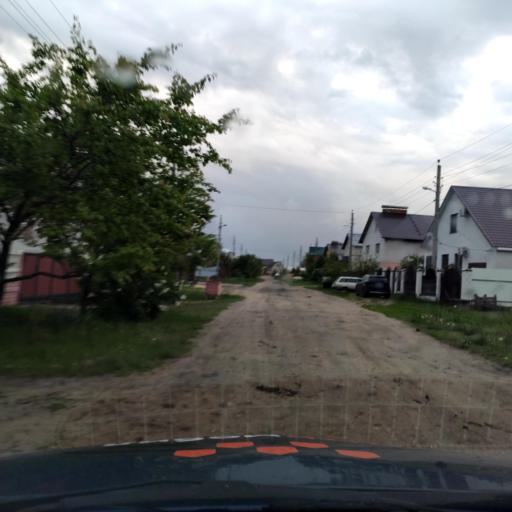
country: RU
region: Voronezj
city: Maslovka
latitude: 51.5440
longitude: 39.2394
